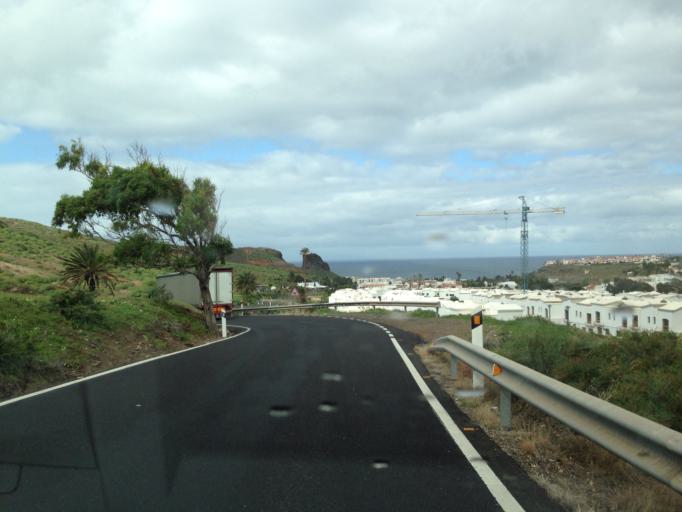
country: ES
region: Canary Islands
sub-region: Provincia de Las Palmas
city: Agaete
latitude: 28.0963
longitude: -15.6998
